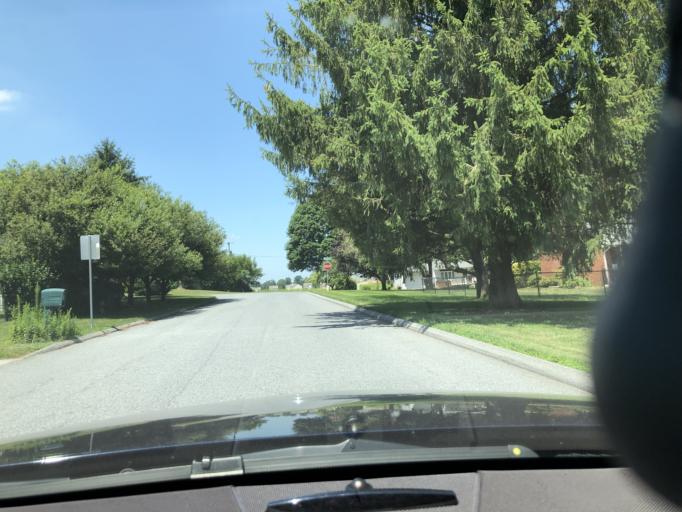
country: US
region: Maryland
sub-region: Carroll County
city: Westminster
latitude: 39.5544
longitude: -76.9667
